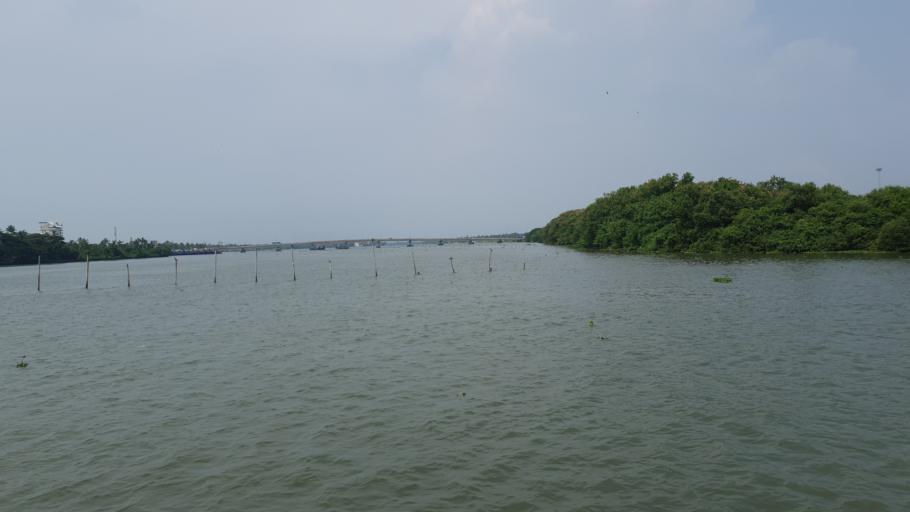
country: IN
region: Kerala
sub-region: Ernakulam
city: Cochin
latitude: 9.9760
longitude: 76.2465
